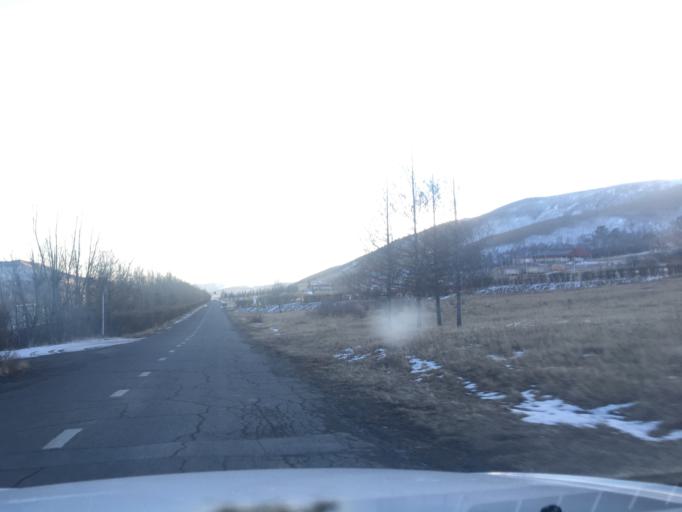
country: MN
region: Ulaanbaatar
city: Ulaanbaatar
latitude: 48.0168
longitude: 106.7311
